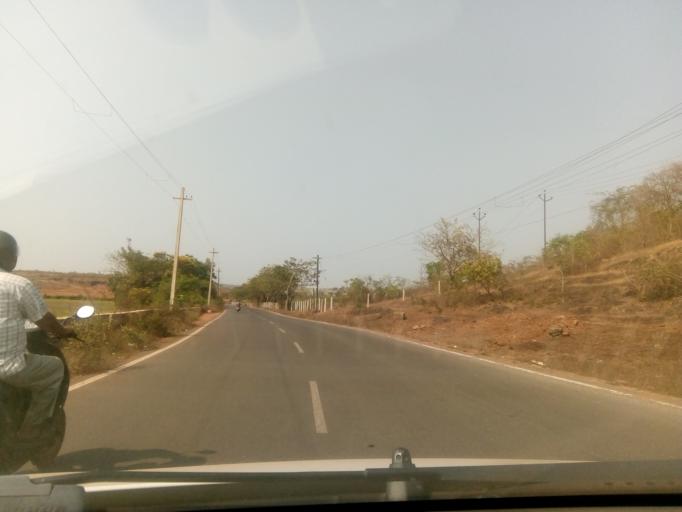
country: IN
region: Goa
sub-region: North Goa
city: Colovale
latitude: 15.6840
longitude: 73.8370
